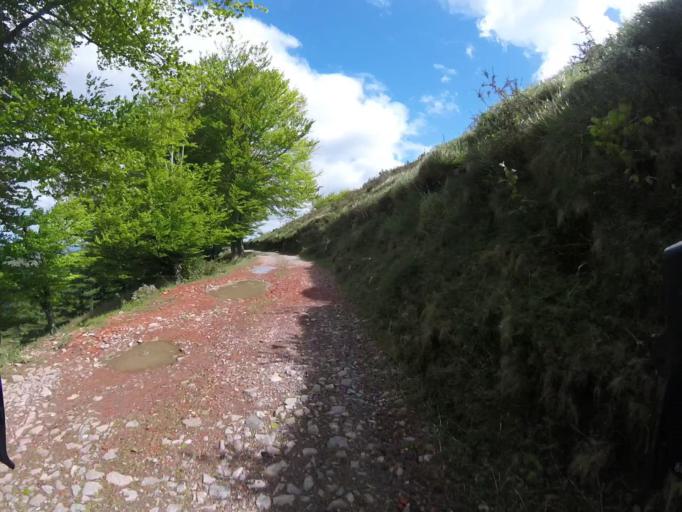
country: ES
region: Navarre
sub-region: Provincia de Navarra
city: Arano
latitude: 43.1832
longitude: -1.9002
